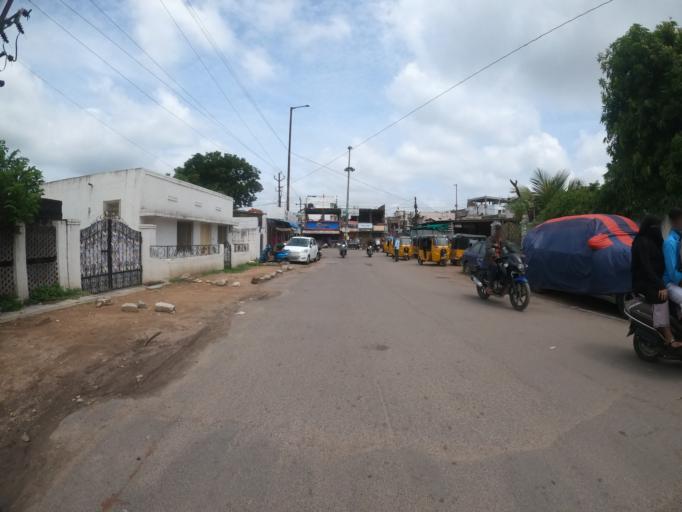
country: IN
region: Telangana
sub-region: Hyderabad
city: Hyderabad
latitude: 17.3927
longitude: 78.4177
